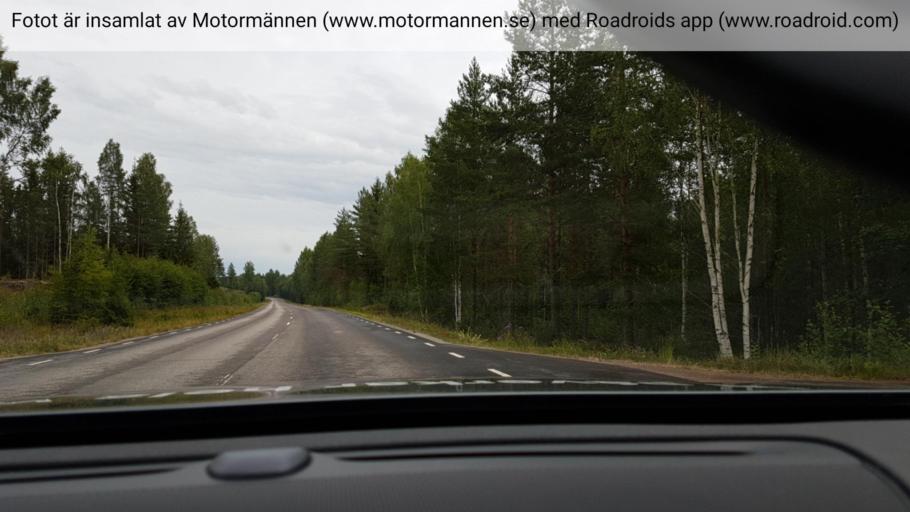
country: SE
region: Dalarna
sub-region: Ludvika Kommun
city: Ludvika
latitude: 60.2902
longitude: 15.2468
